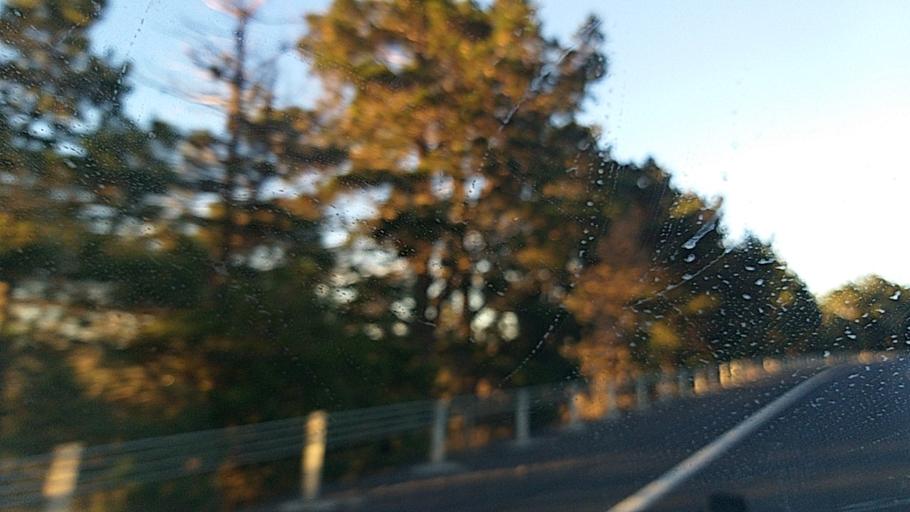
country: AU
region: New South Wales
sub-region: Goulburn Mulwaree
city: Goulburn
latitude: -34.8742
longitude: 149.5431
